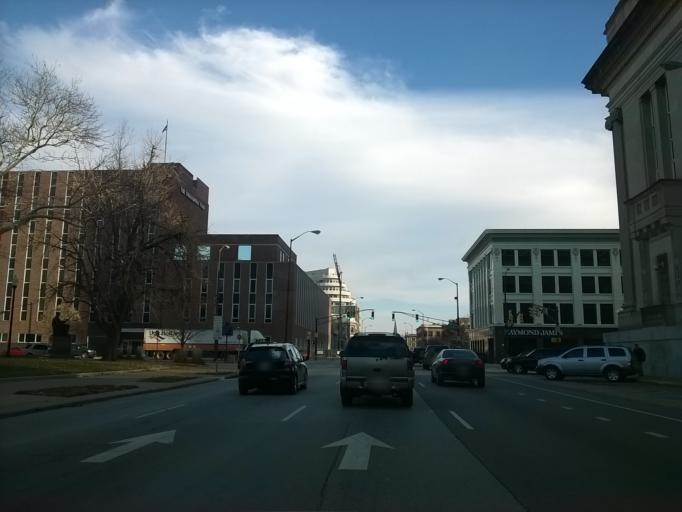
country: US
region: Indiana
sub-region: Marion County
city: Indianapolis
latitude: 39.7713
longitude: -86.1569
